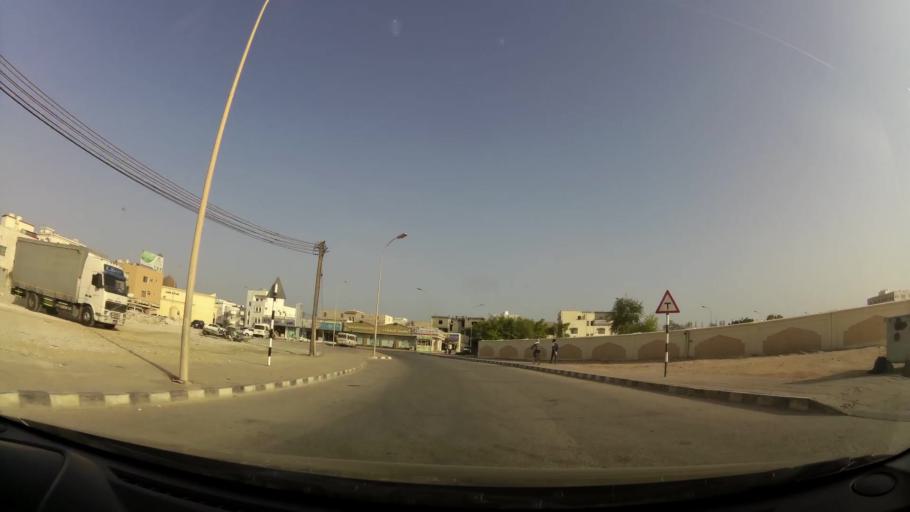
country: OM
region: Zufar
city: Salalah
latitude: 17.0124
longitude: 54.0901
